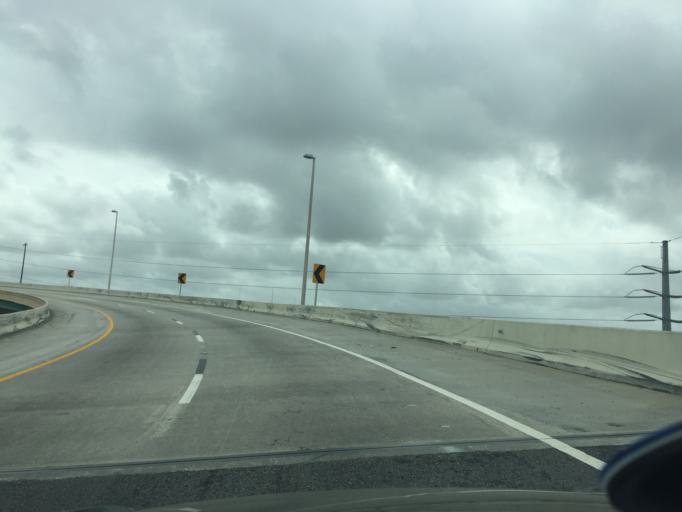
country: US
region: Florida
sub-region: Broward County
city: Broadview Park
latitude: 26.0874
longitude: -80.2202
